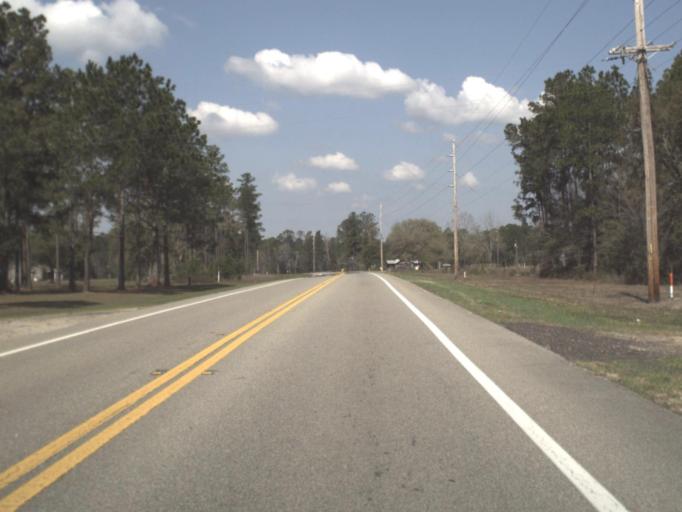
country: US
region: Florida
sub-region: Liberty County
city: Bristol
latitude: 30.4012
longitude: -84.8150
